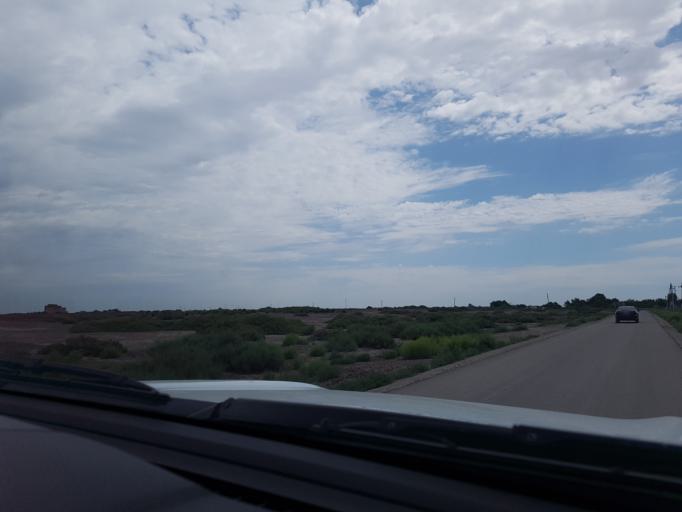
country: TM
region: Dasoguz
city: Koeneuergench
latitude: 42.2946
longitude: 59.1416
